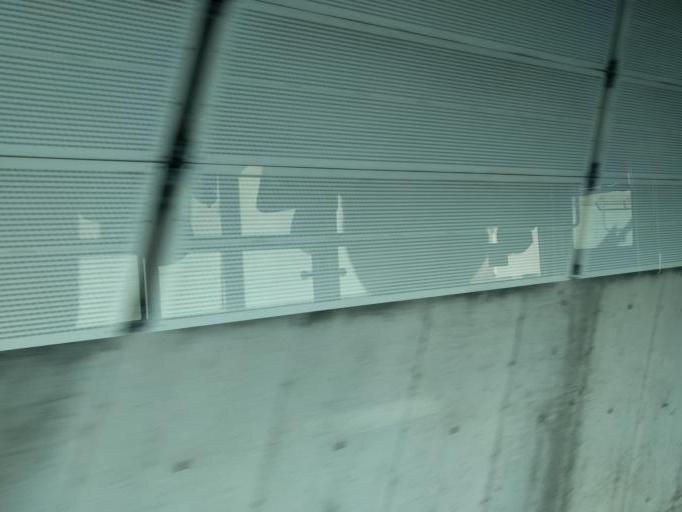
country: JP
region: Hyogo
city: Kobe
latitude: 34.7018
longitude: 135.1985
